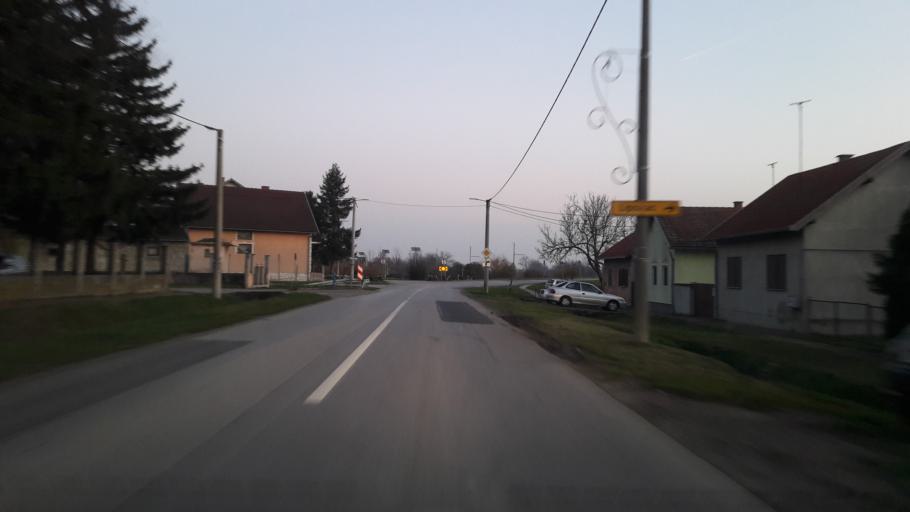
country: HR
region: Vukovarsko-Srijemska
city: Nijemci
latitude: 45.1431
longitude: 19.0367
